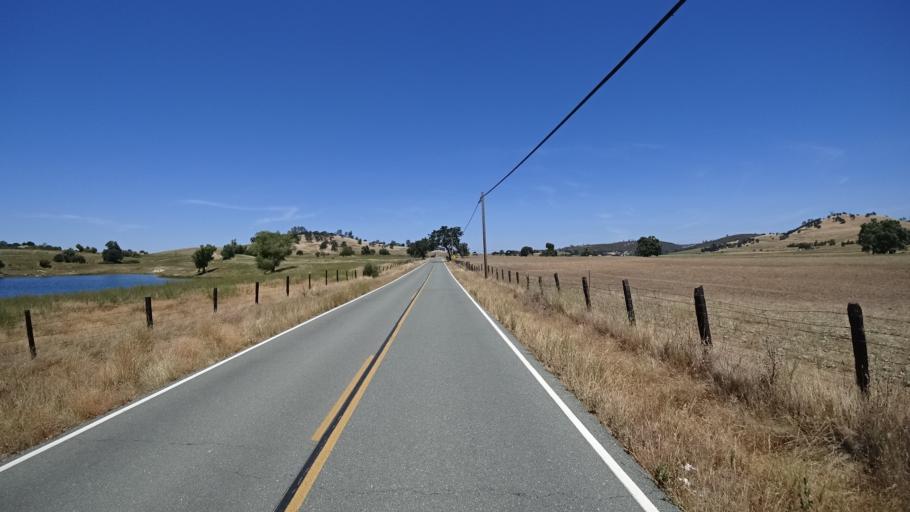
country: US
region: California
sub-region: Calaveras County
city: Valley Springs
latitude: 38.2152
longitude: -120.8252
